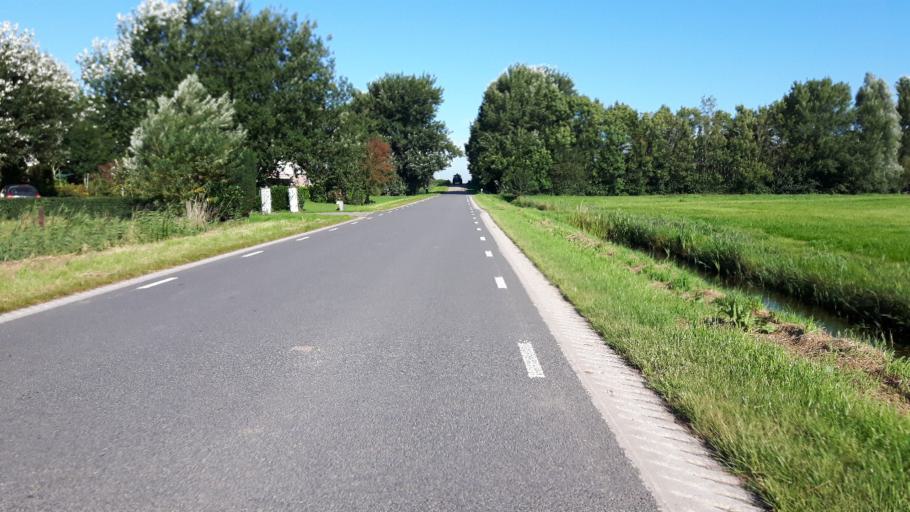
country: NL
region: Overijssel
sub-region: Gemeente Steenwijkerland
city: Oldemarkt
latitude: 52.8118
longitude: 5.9102
